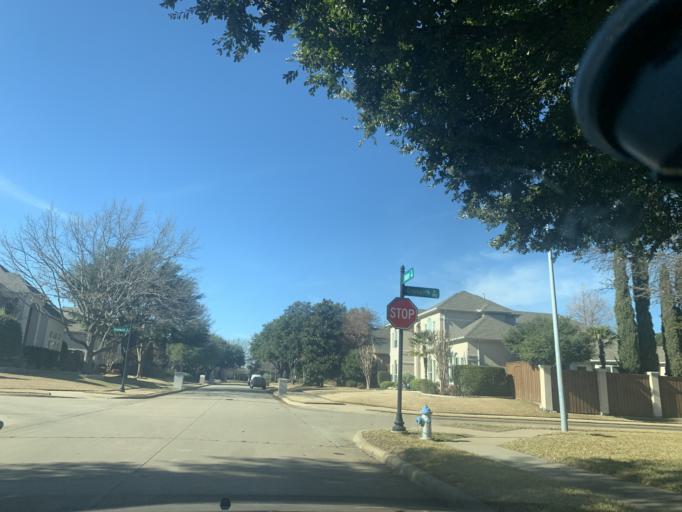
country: US
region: Texas
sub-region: Denton County
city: The Colony
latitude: 33.0521
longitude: -96.8141
